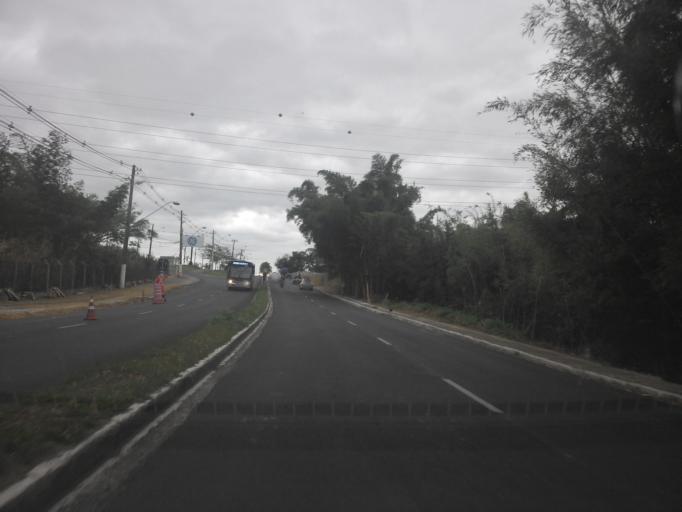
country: BR
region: Sao Paulo
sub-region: Taubate
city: Taubate
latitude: -23.0266
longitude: -45.5980
